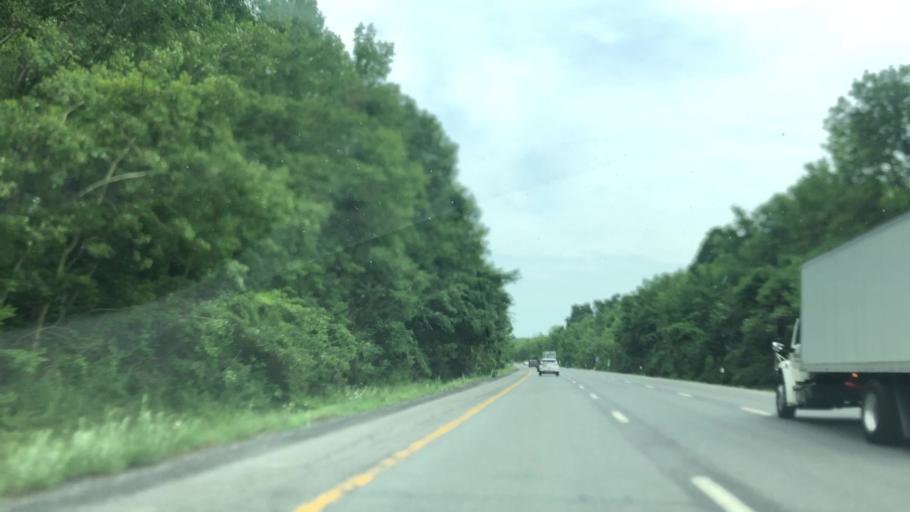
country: US
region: New York
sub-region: Saratoga County
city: Saratoga Springs
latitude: 43.0284
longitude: -73.7838
